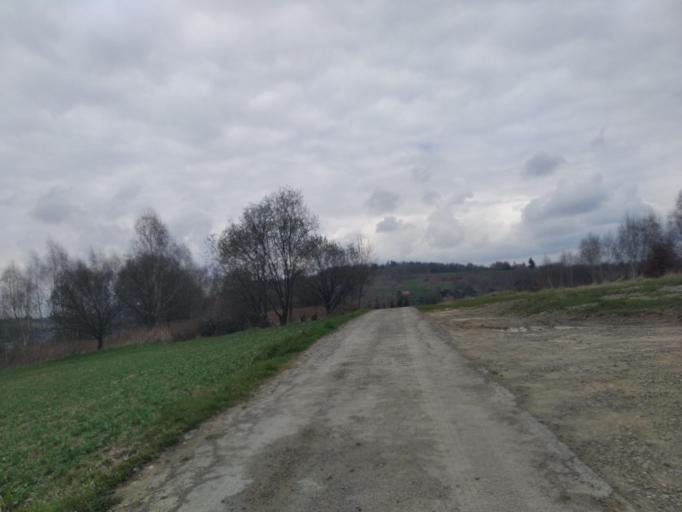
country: PL
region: Subcarpathian Voivodeship
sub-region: Powiat strzyzowski
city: Wysoka Strzyzowska
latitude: 49.8829
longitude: 21.7188
